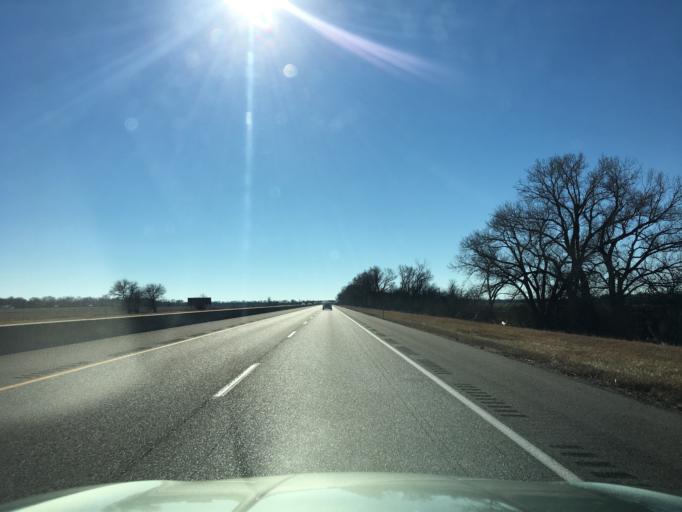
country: US
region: Kansas
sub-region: Sumner County
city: Belle Plaine
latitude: 37.4457
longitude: -97.3220
